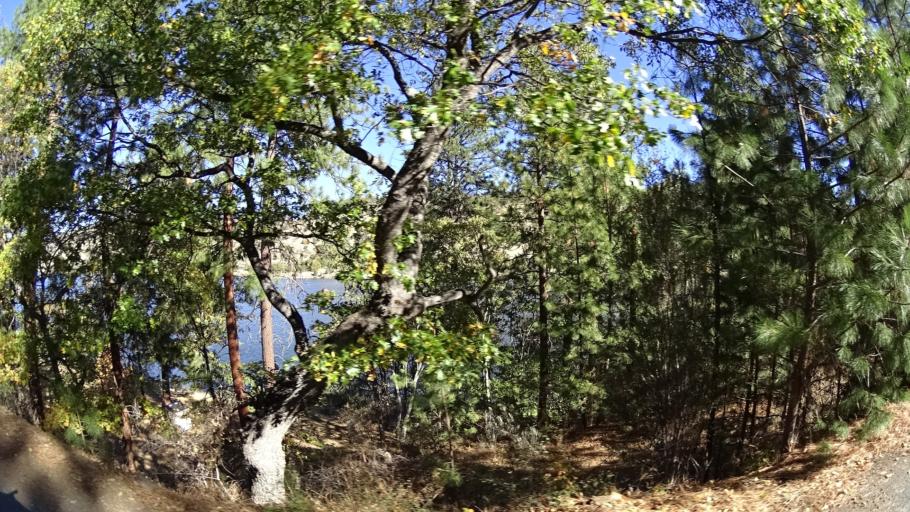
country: US
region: California
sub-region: Siskiyou County
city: Montague
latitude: 41.9742
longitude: -122.2921
